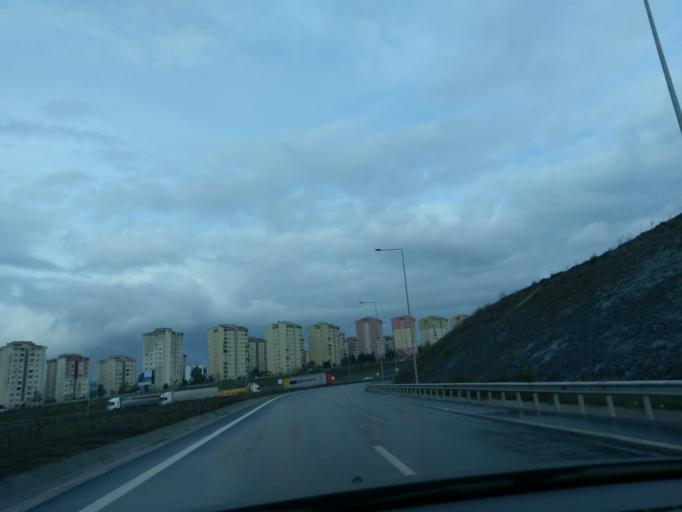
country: TR
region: Istanbul
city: Basaksehir
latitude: 41.0843
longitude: 28.8147
